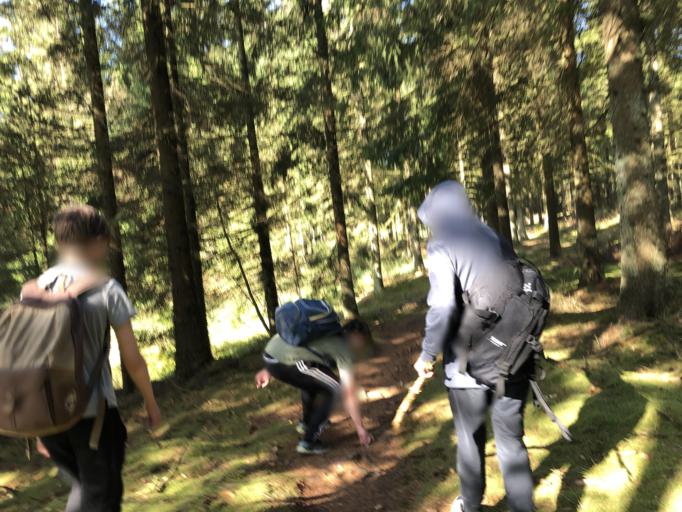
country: DK
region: Central Jutland
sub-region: Lemvig Kommune
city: Lemvig
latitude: 56.4777
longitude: 8.3324
